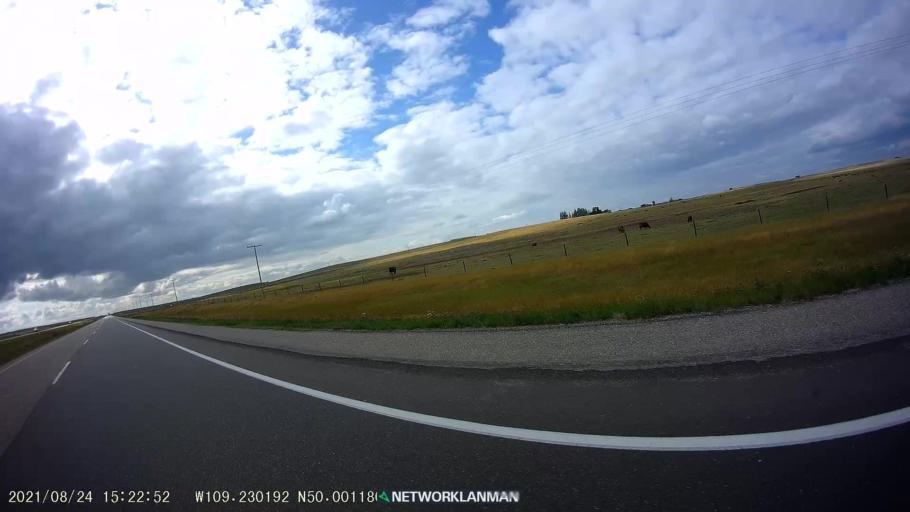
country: CA
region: Saskatchewan
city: Maple Creek
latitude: 50.0013
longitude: -109.2305
